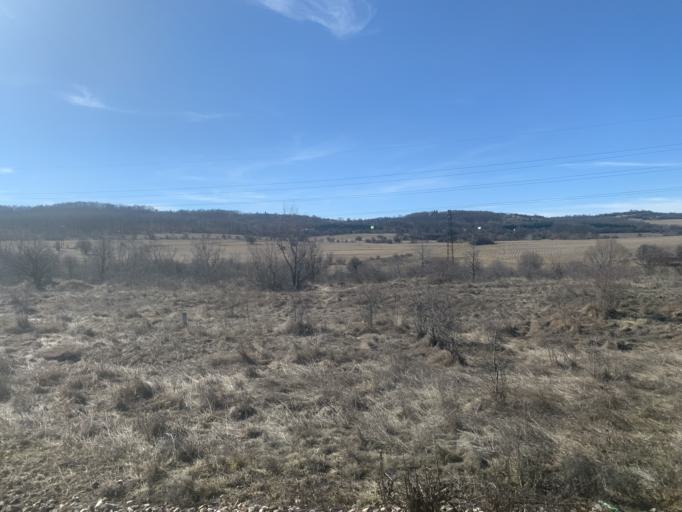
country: BG
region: Sofiya
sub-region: Obshtina Gorna Malina
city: Gorna Malina
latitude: 42.5611
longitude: 23.6945
